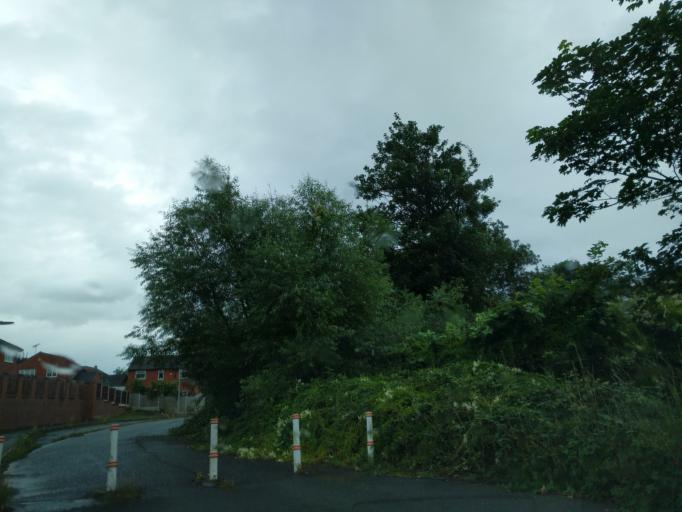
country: GB
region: England
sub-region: Staffordshire
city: Stafford
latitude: 52.8075
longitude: -2.0861
